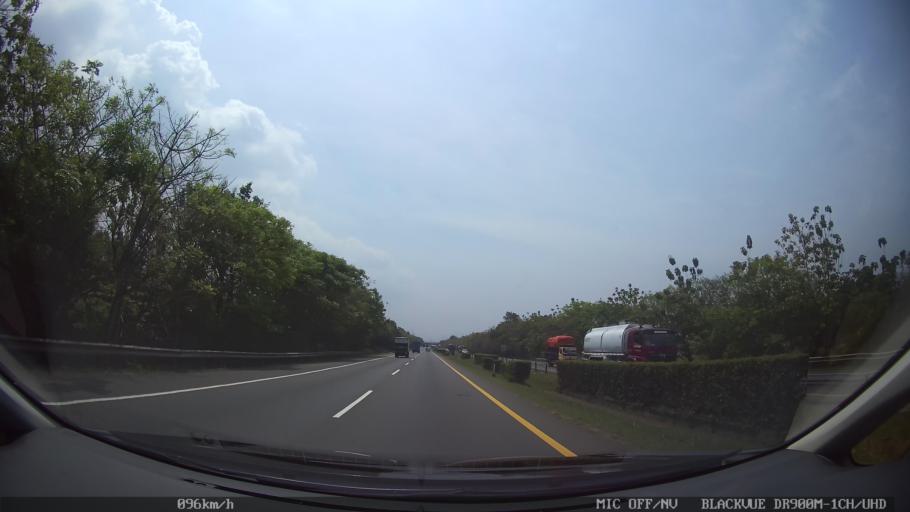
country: ID
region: Banten
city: Serang
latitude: -6.0706
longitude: 106.1281
